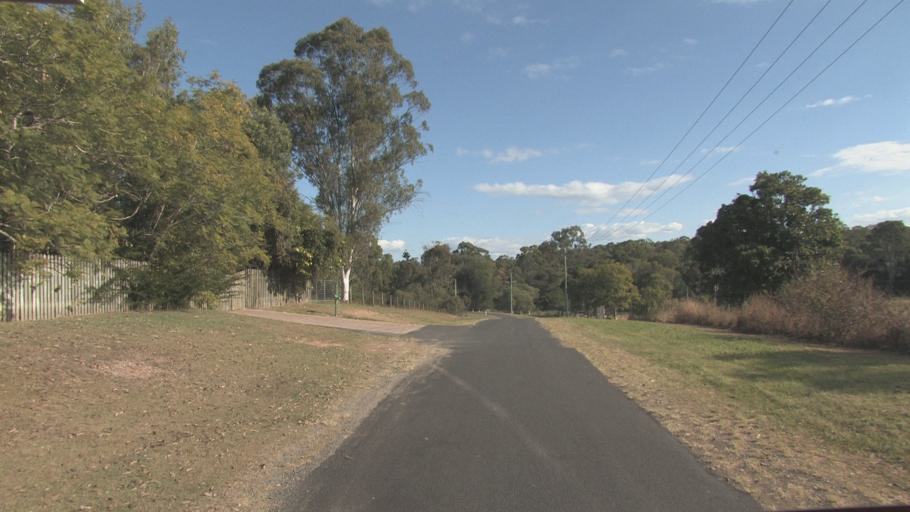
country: AU
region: Queensland
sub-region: Logan
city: Windaroo
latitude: -27.7427
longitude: 153.1621
